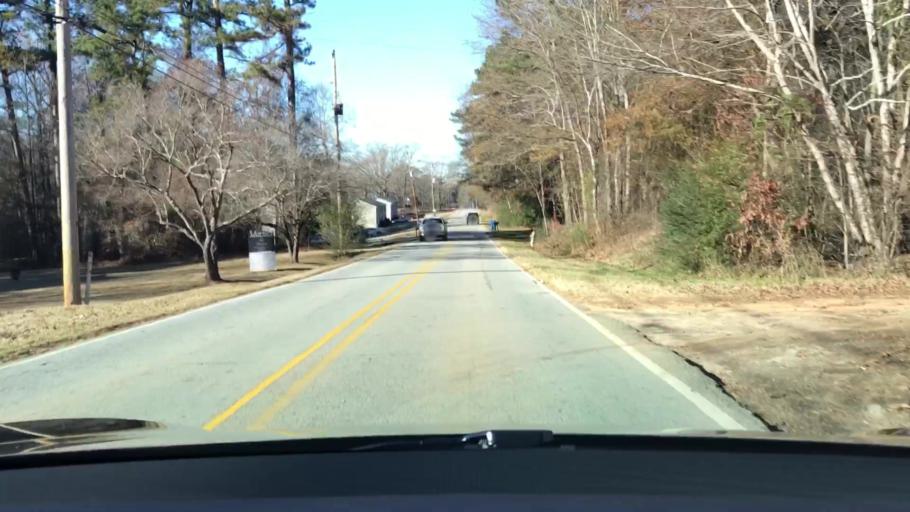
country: US
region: Georgia
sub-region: Barrow County
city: Auburn
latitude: 34.0167
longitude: -83.8287
